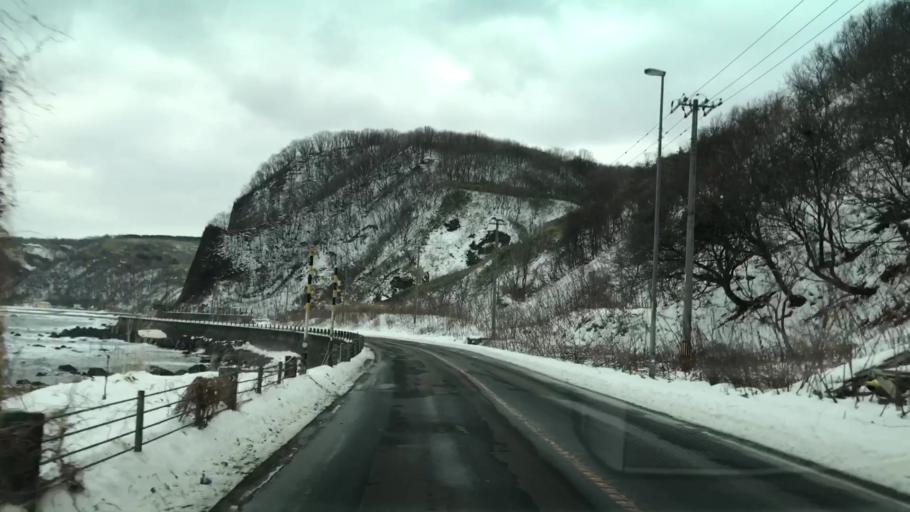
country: JP
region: Hokkaido
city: Iwanai
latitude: 43.3307
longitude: 140.4156
